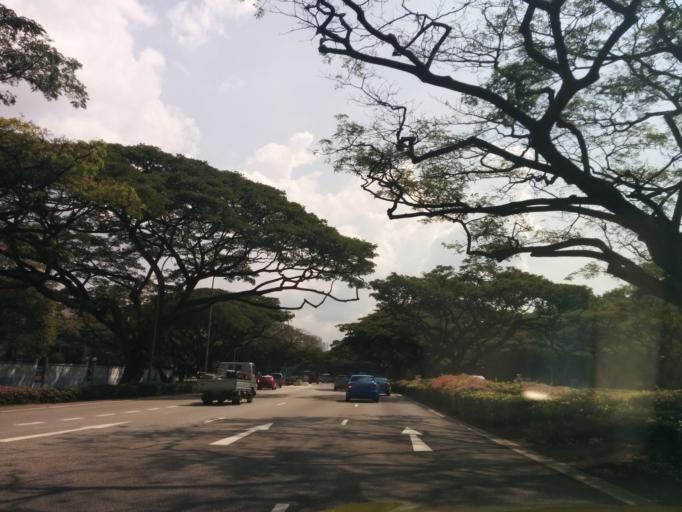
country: SG
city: Singapore
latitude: 1.3058
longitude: 103.9253
